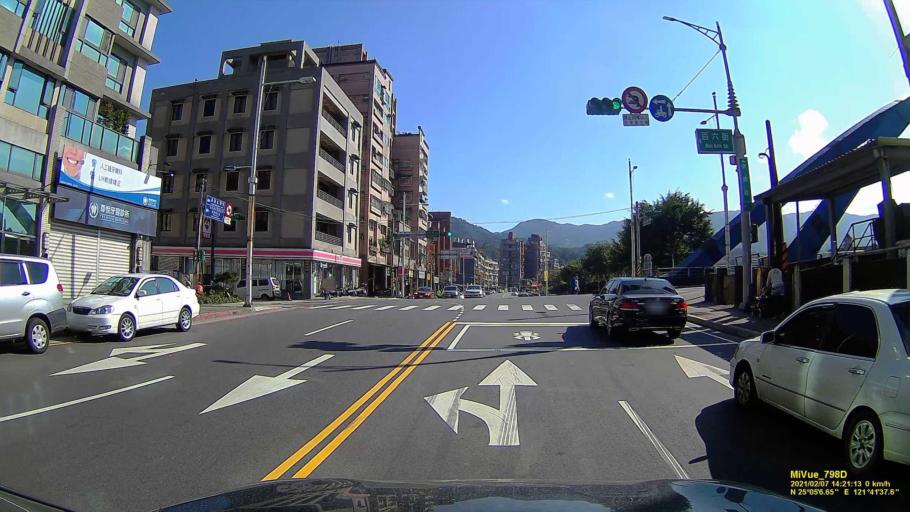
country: TW
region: Taiwan
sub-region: Keelung
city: Keelung
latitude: 25.0851
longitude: 121.6938
